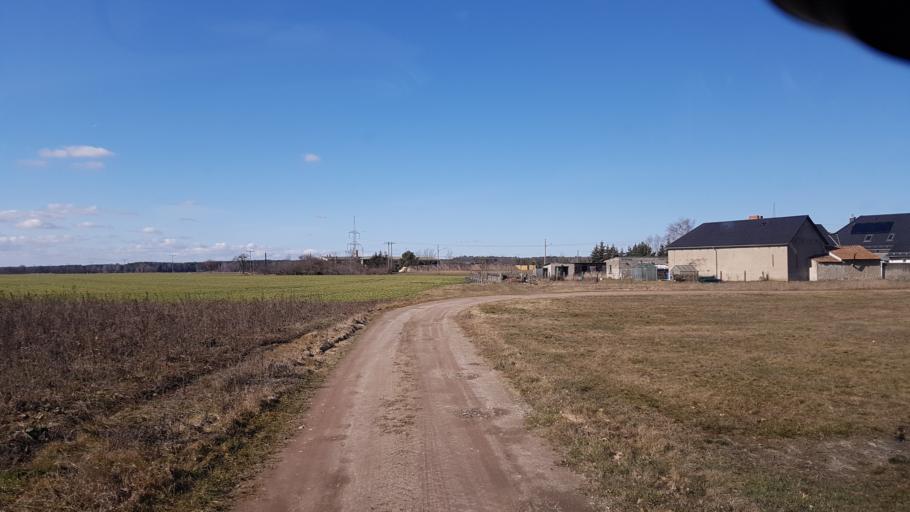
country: DE
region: Brandenburg
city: Schonborn
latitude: 51.5666
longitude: 13.5137
